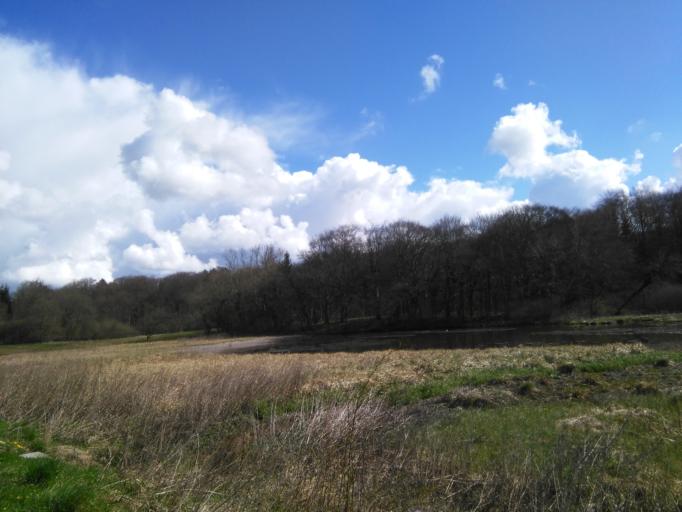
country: DK
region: Central Jutland
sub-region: Arhus Kommune
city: Trige
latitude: 56.2341
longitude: 10.1669
